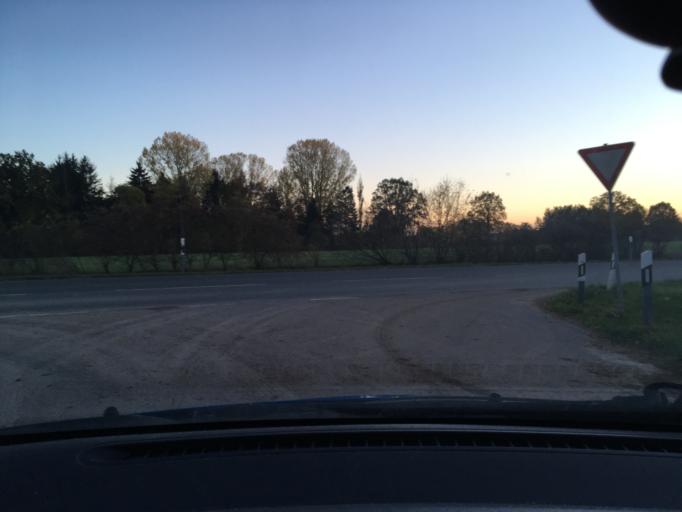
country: DE
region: Lower Saxony
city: Radbruch
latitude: 53.3217
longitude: 10.2952
